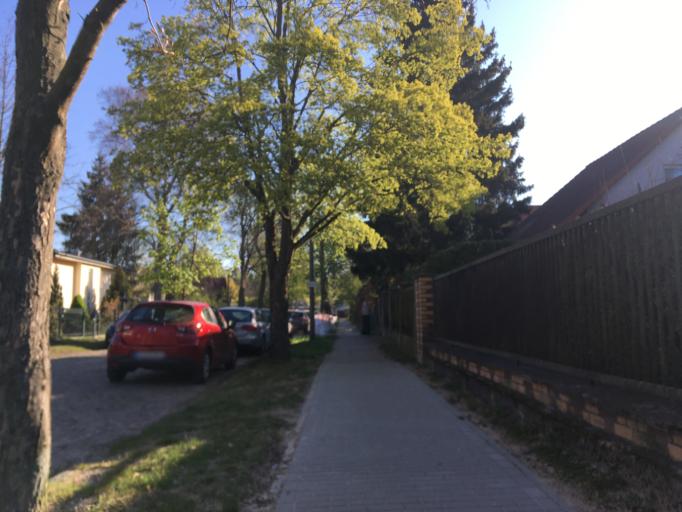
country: DE
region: Berlin
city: Buch
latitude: 52.6453
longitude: 13.5059
